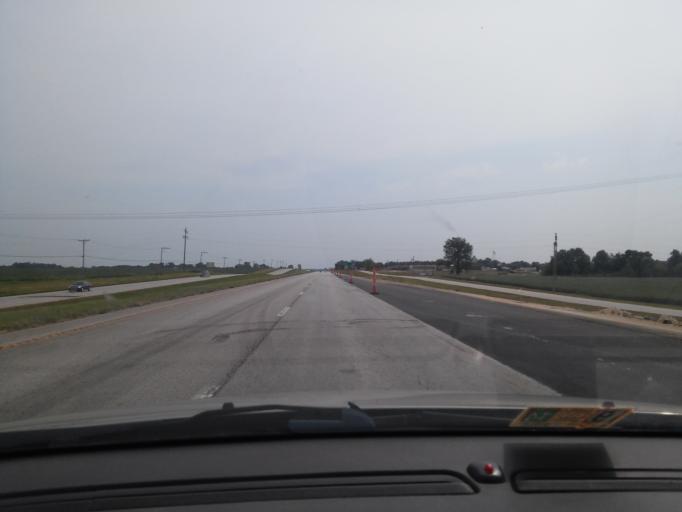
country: US
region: Missouri
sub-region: Callaway County
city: Fulton
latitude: 38.9597
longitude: -91.9261
